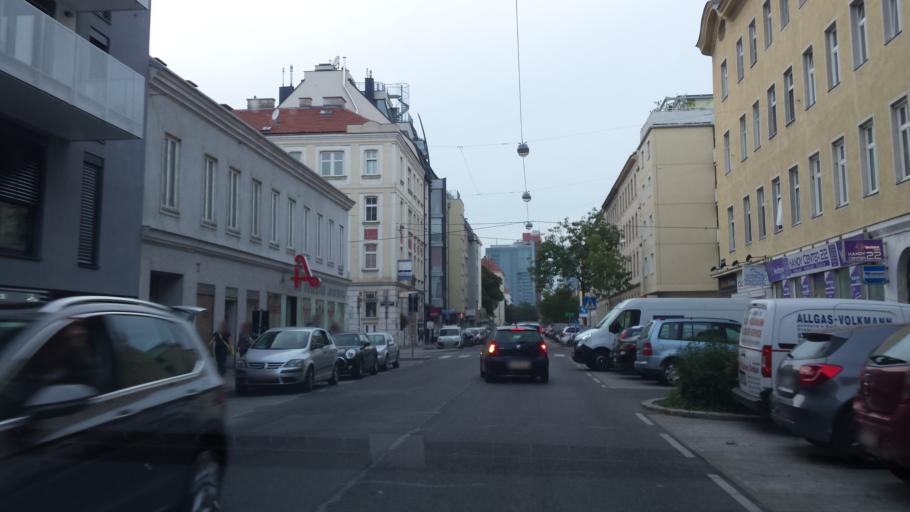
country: AT
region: Vienna
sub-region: Wien Stadt
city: Vienna
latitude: 48.2269
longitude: 16.4223
